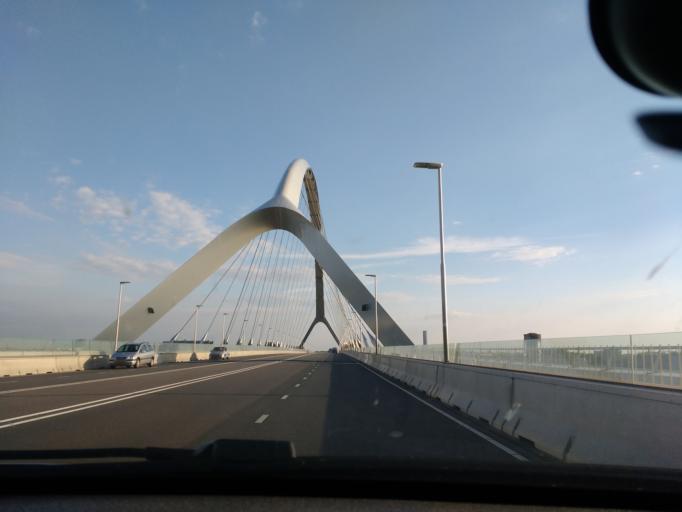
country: NL
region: Gelderland
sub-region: Gemeente Nijmegen
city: Nijmegen
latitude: 51.8598
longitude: 5.8422
